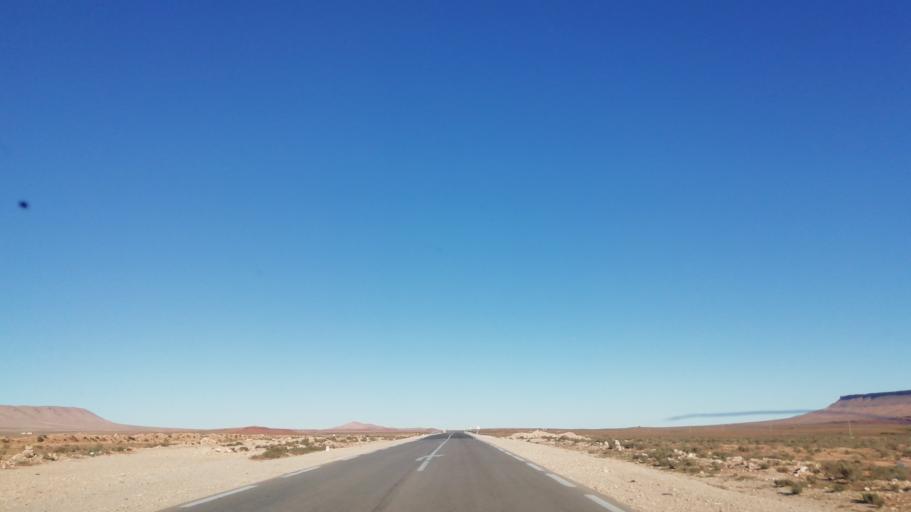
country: DZ
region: El Bayadh
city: El Abiodh Sidi Cheikh
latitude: 33.0833
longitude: 0.1759
